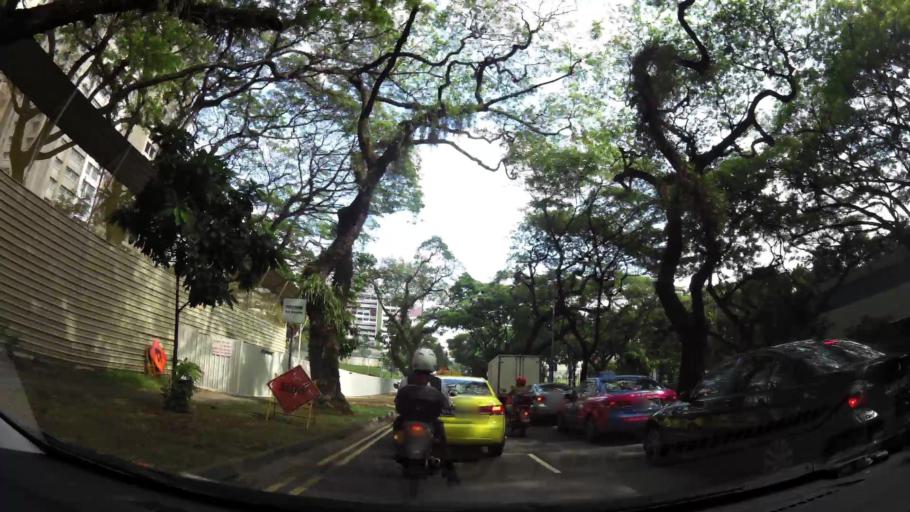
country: SG
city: Singapore
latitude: 1.2875
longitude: 103.8225
